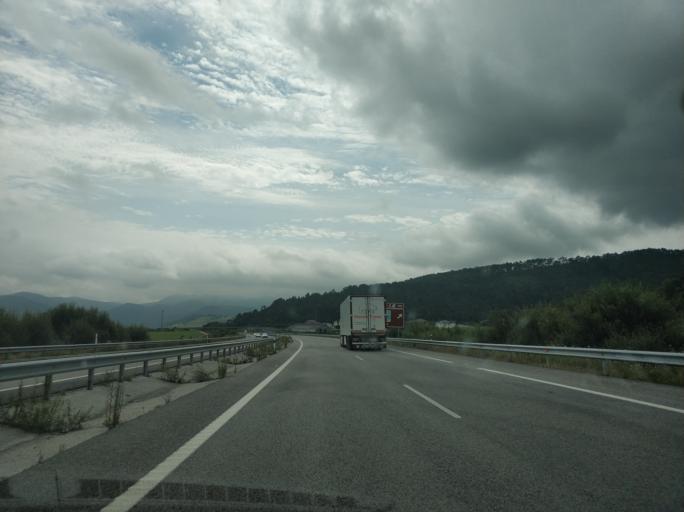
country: ES
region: Asturias
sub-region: Province of Asturias
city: Navia
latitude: 43.5318
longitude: -6.5837
